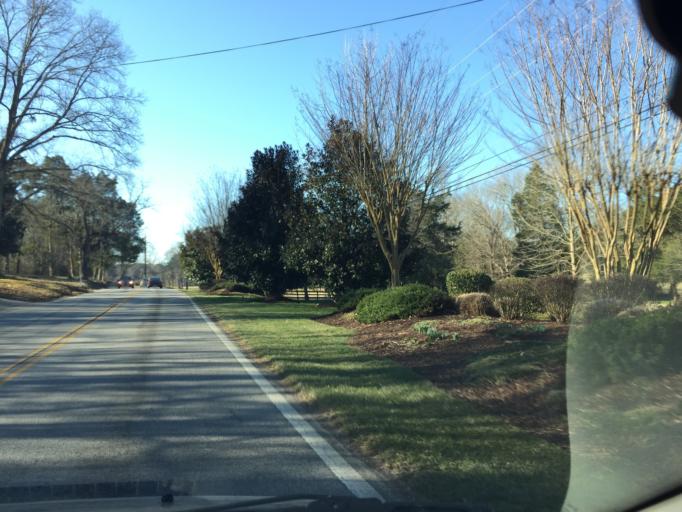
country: US
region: Tennessee
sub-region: Hamilton County
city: Collegedale
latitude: 35.0535
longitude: -85.0702
